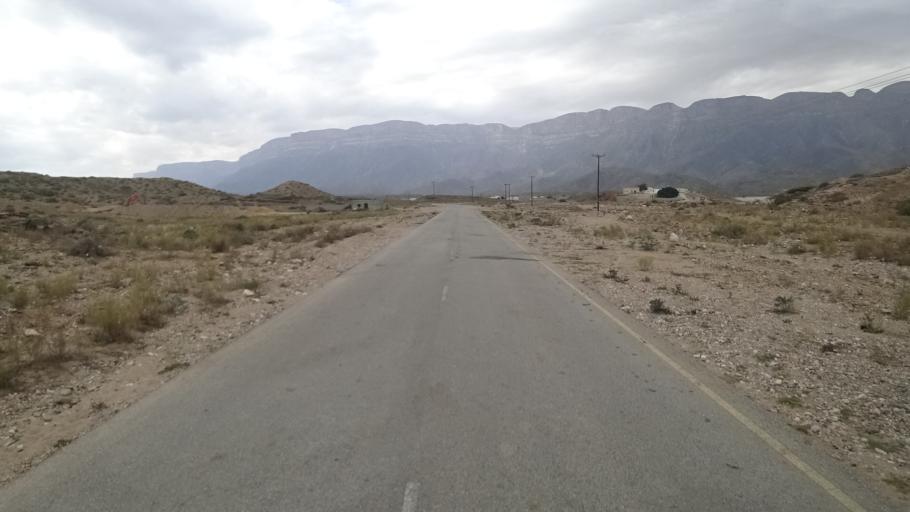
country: OM
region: Zufar
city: Salalah
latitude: 17.1604
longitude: 54.9930
